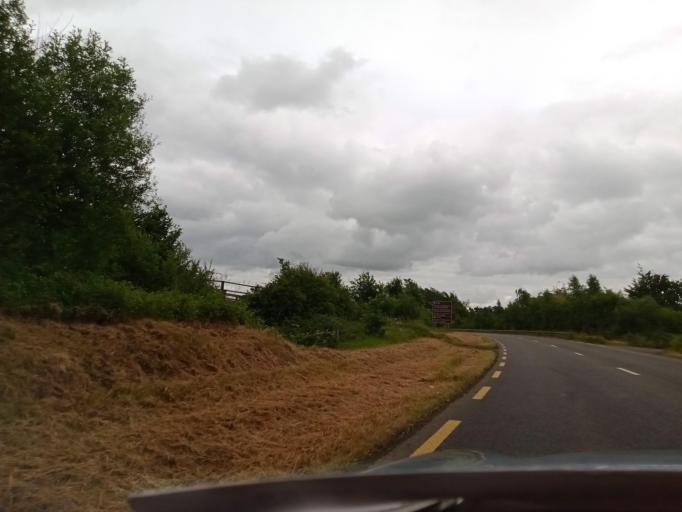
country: IE
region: Leinster
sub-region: Kilkenny
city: Thomastown
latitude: 52.4851
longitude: -7.2240
